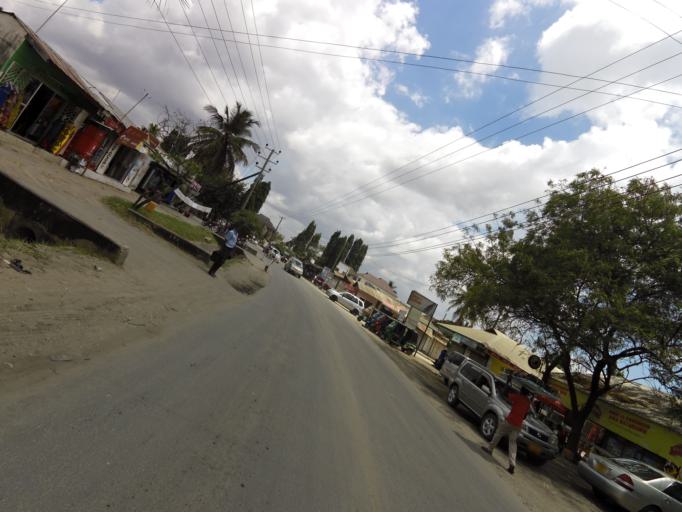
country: TZ
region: Dar es Salaam
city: Magomeni
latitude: -6.7864
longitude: 39.2260
